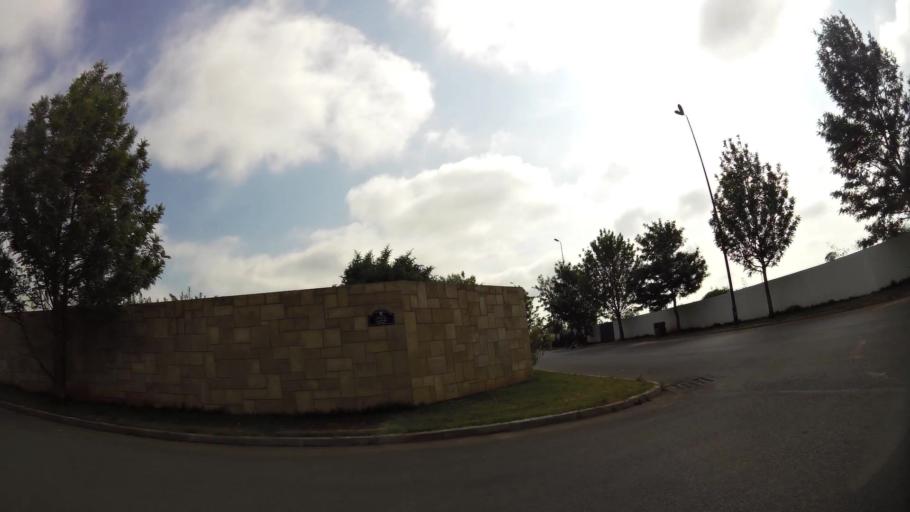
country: MA
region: Rabat-Sale-Zemmour-Zaer
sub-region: Rabat
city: Rabat
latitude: 33.9724
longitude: -6.8493
